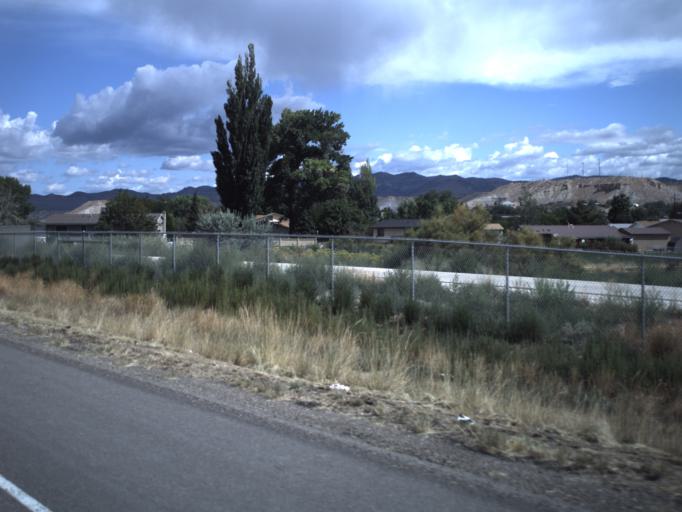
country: US
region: Utah
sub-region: Carbon County
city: Price
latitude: 39.5938
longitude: -110.8217
